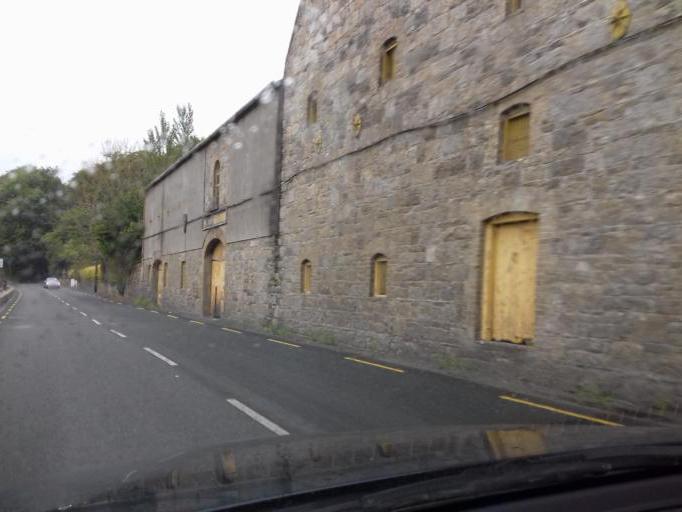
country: IE
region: Leinster
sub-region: County Carlow
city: Bagenalstown
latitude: 52.7078
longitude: -6.9540
